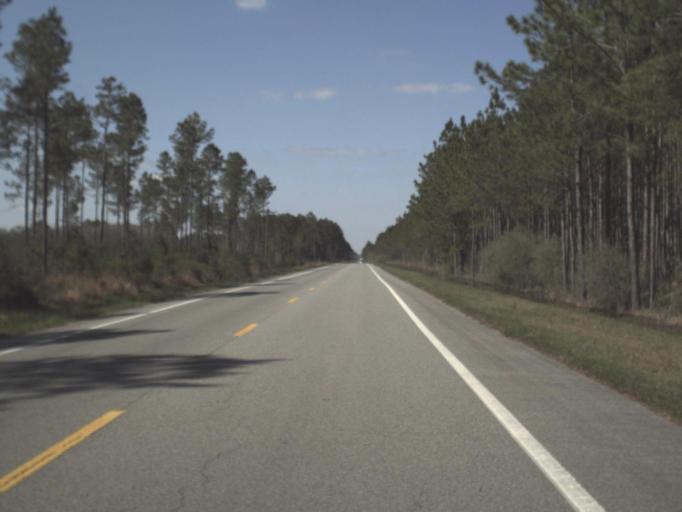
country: US
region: Florida
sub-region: Gulf County
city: Wewahitchka
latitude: 30.0054
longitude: -85.1740
